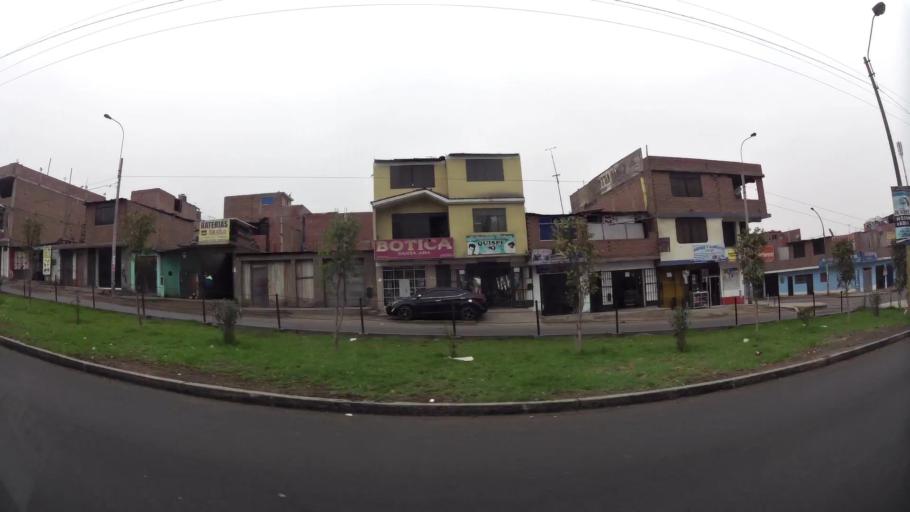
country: PE
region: Lima
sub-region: Lima
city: Urb. Santo Domingo
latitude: -11.9392
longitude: -76.9779
